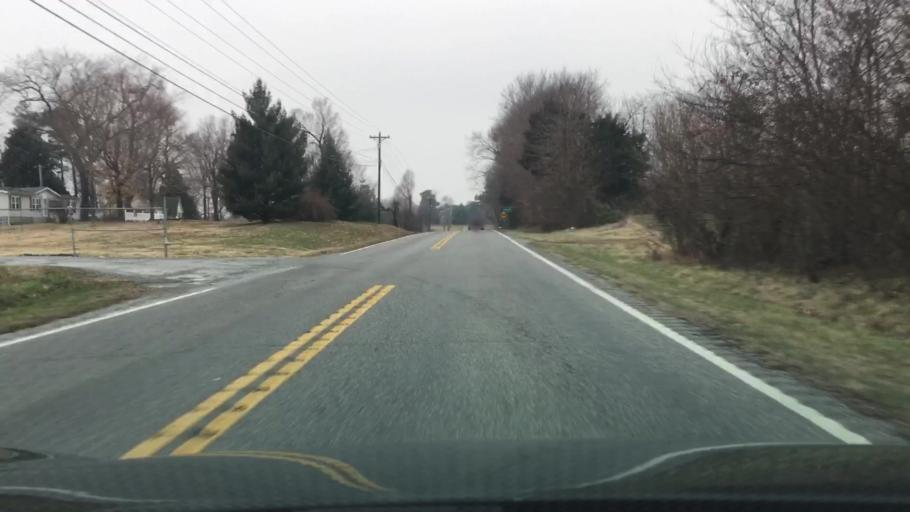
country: US
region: Kentucky
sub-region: Livingston County
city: Ledbetter
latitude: 36.9667
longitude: -88.4460
